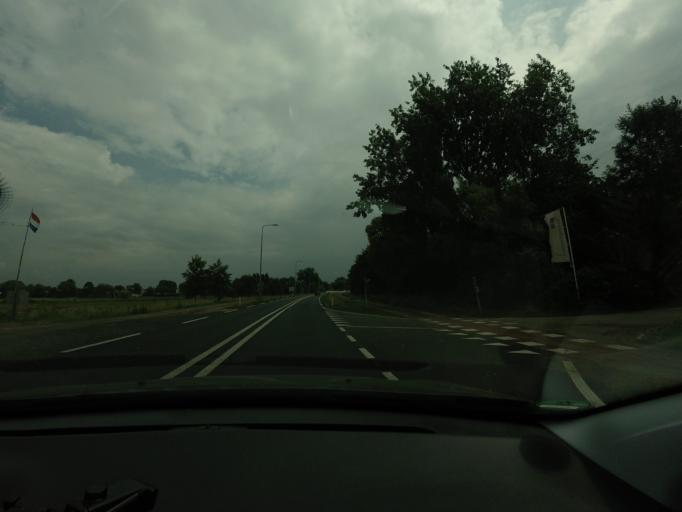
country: NL
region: Gelderland
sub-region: Gemeente Tiel
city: Tiel
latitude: 51.8863
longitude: 5.3981
